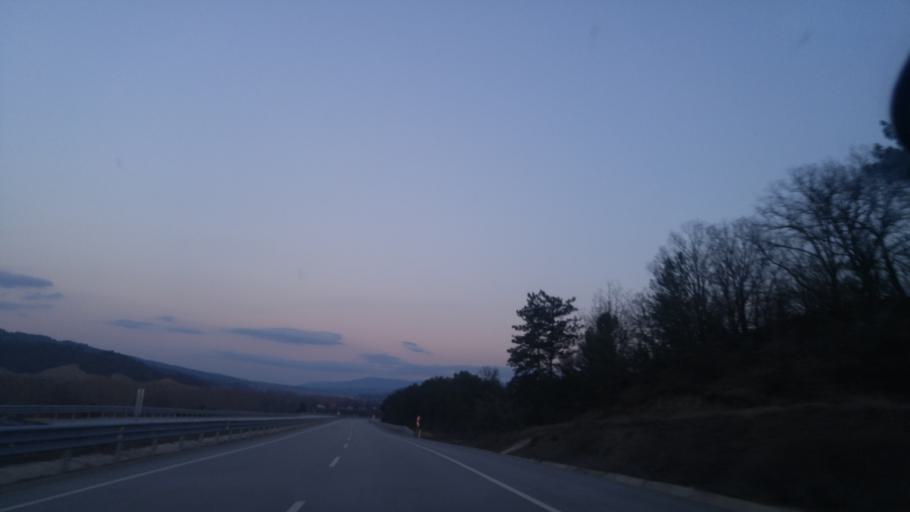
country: TR
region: Kastamonu
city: Igdir
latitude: 41.2326
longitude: 33.0698
